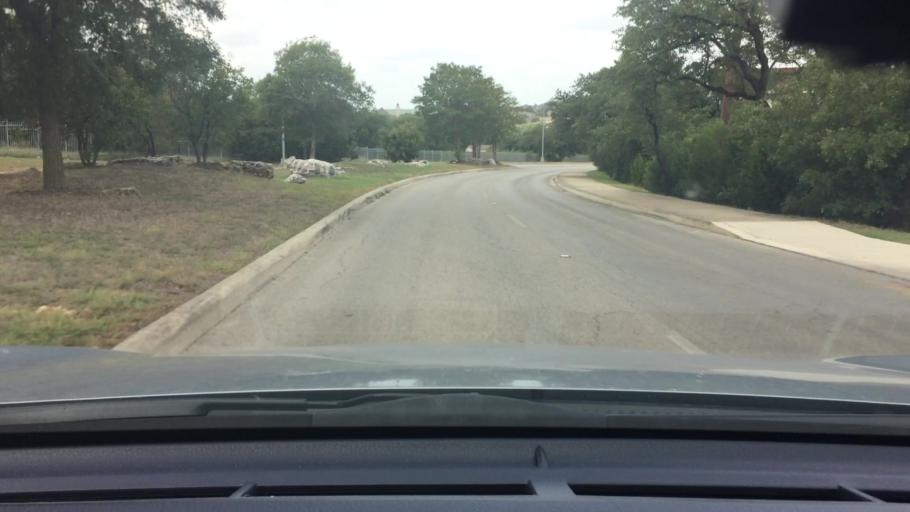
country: US
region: Texas
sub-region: Bexar County
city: Timberwood Park
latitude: 29.6609
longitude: -98.5011
